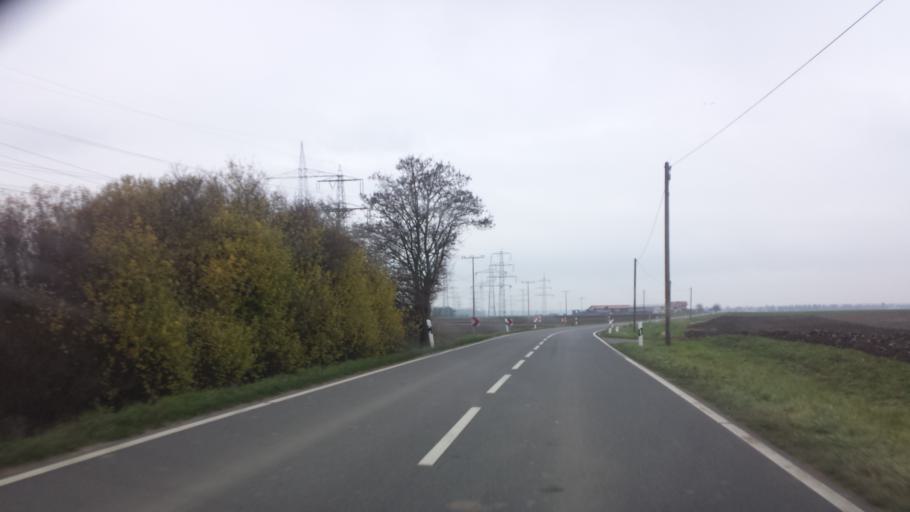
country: DE
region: Rheinland-Pfalz
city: Worms
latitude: 49.6602
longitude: 8.3947
